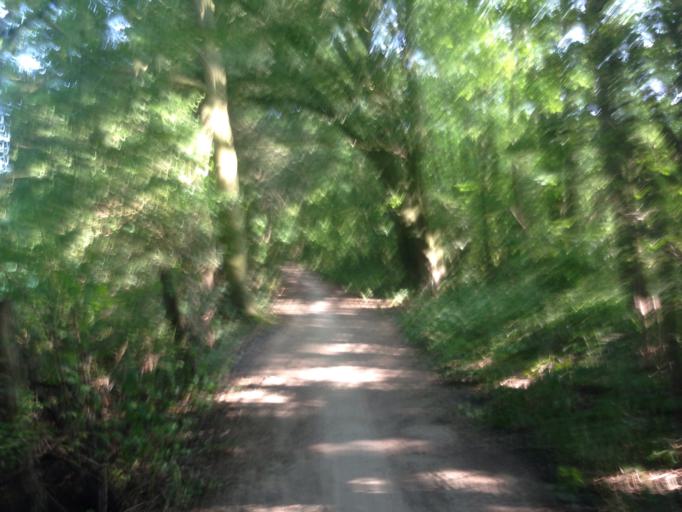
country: DE
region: North Rhine-Westphalia
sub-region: Regierungsbezirk Munster
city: Muenster
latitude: 52.0121
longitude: 7.5666
